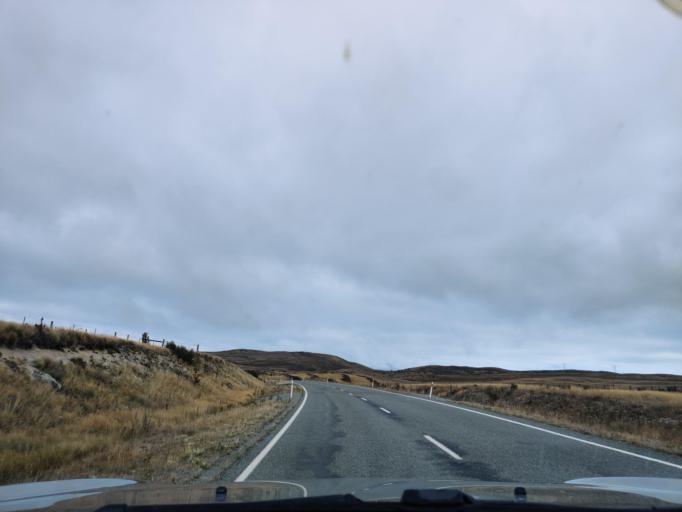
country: NZ
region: Canterbury
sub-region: Timaru District
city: Pleasant Point
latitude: -44.1811
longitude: 170.2292
